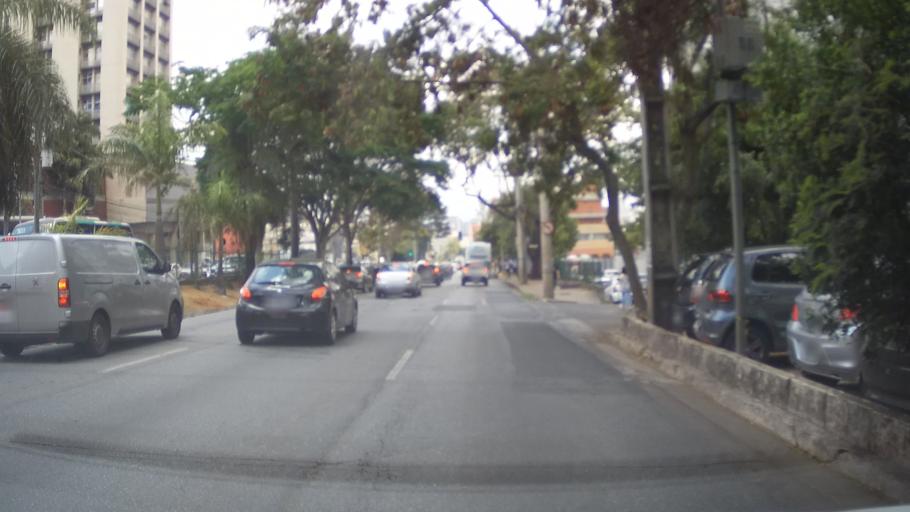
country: BR
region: Minas Gerais
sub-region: Belo Horizonte
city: Belo Horizonte
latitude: -19.9547
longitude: -43.9398
